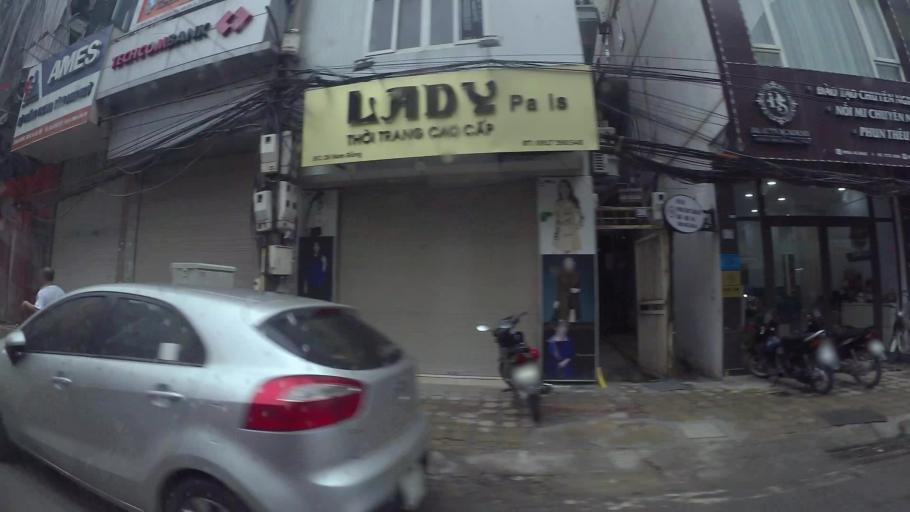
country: VN
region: Ha Noi
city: Dong Da
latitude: 21.0138
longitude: 105.8335
